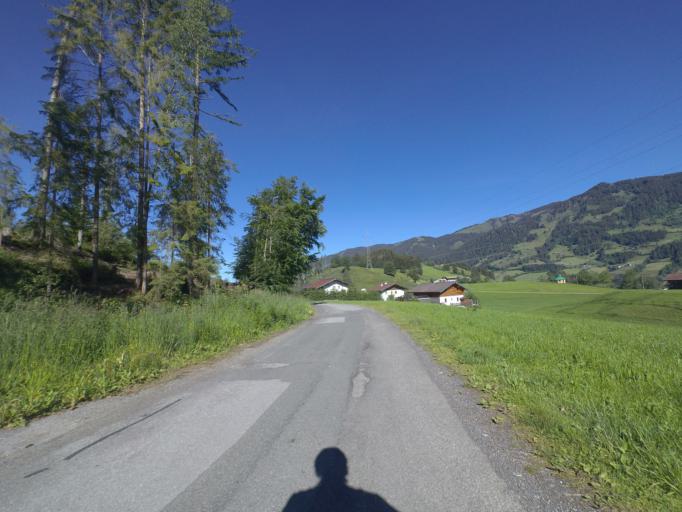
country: AT
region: Salzburg
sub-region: Politischer Bezirk Sankt Johann im Pongau
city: Goldegg
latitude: 47.3243
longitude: 13.1145
